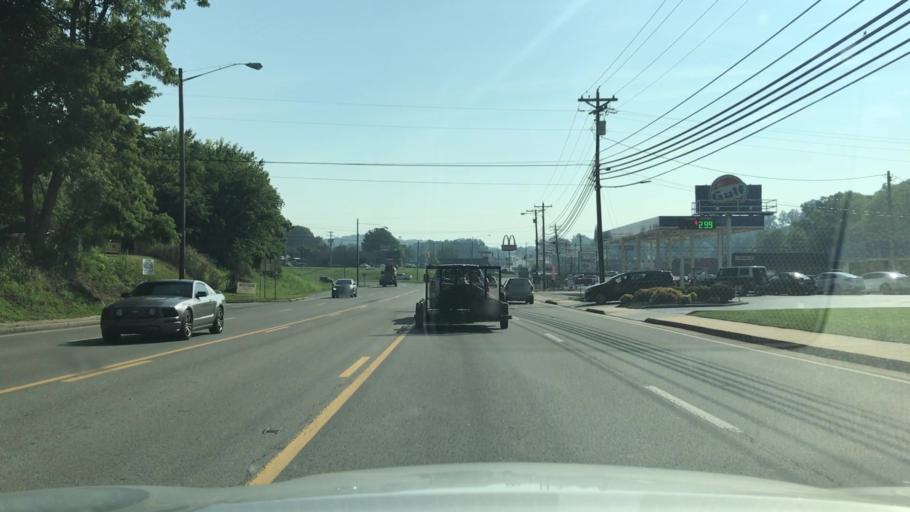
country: US
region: Tennessee
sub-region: Overton County
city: Livingston
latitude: 36.3773
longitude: -85.3362
